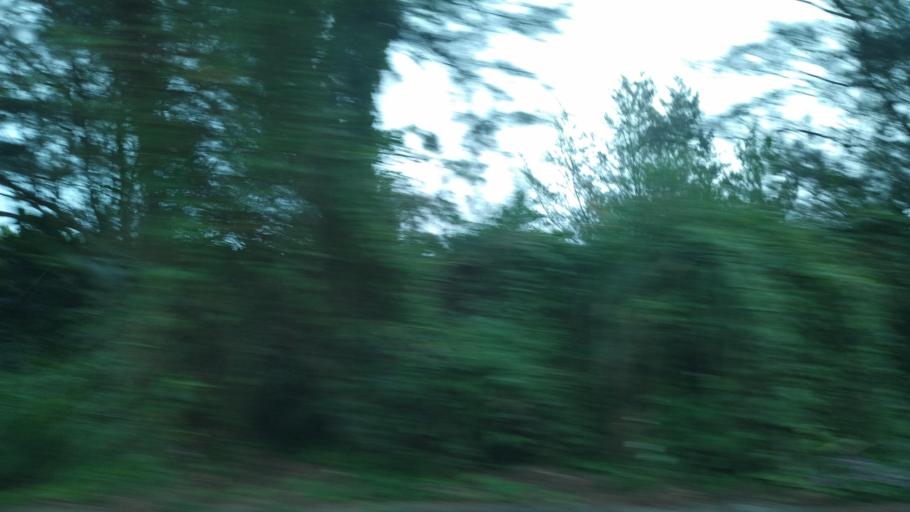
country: TW
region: Taiwan
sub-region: Keelung
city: Keelung
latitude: 25.2193
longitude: 121.6475
